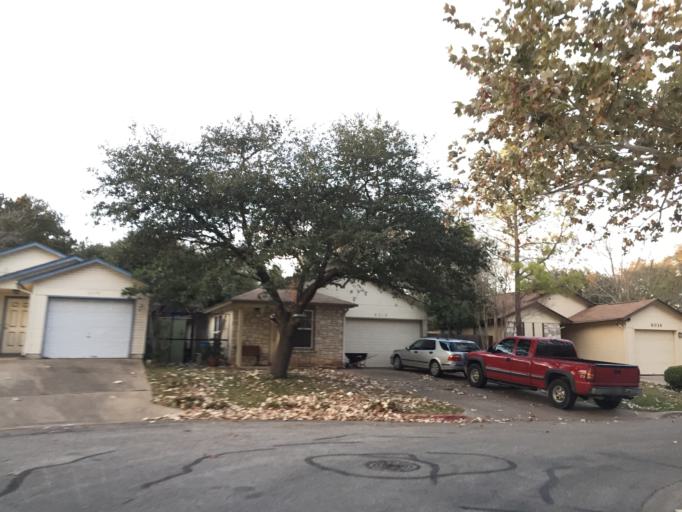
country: US
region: Texas
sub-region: Williamson County
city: Jollyville
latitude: 30.4397
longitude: -97.7440
